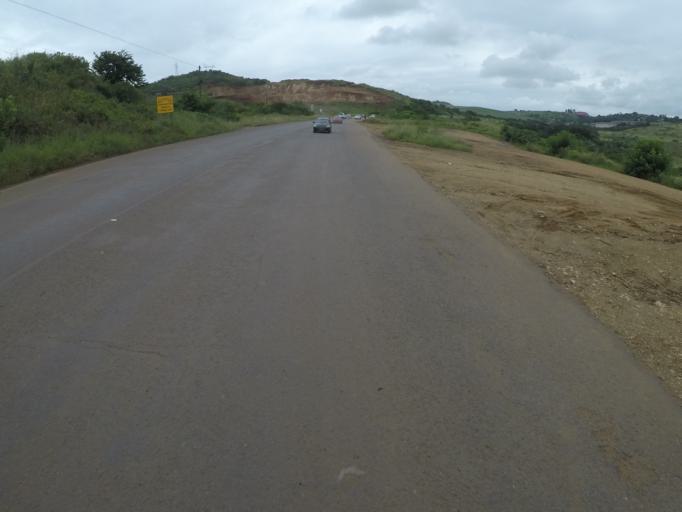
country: ZA
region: KwaZulu-Natal
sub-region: uThungulu District Municipality
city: Empangeni
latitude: -28.7574
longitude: 31.8742
